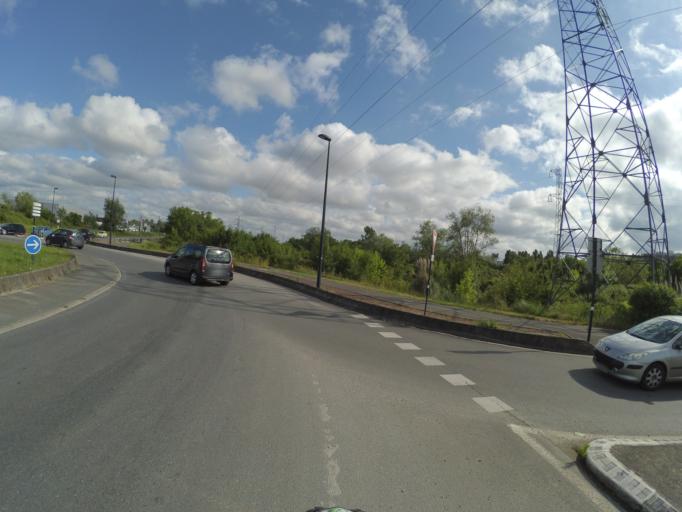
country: FR
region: Aquitaine
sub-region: Departement de la Gironde
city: Bassens
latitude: 44.8962
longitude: -0.5510
